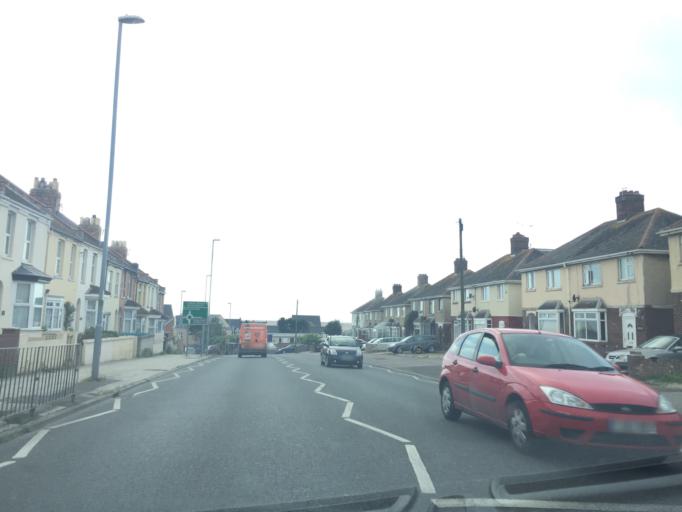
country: GB
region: England
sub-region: Dorset
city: Weymouth
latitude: 50.5876
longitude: -2.4725
